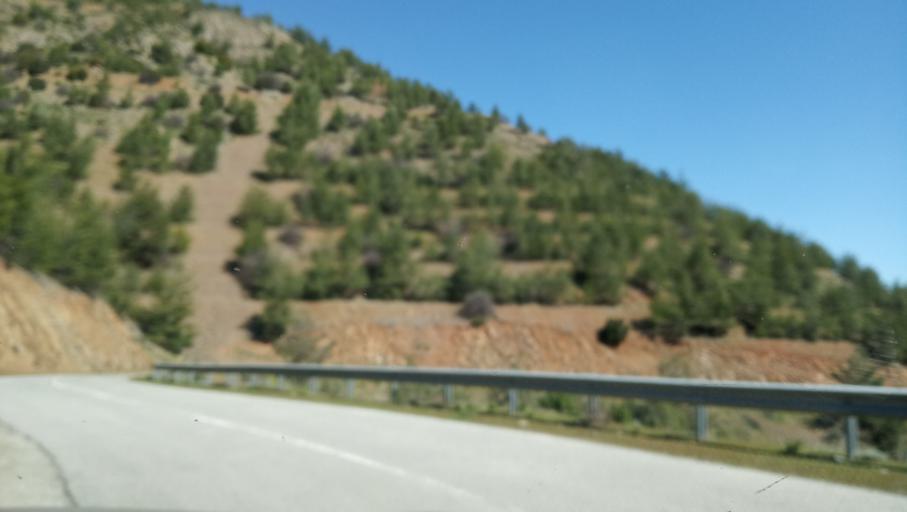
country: CY
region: Lefkosia
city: Lefka
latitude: 35.0793
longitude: 32.7724
